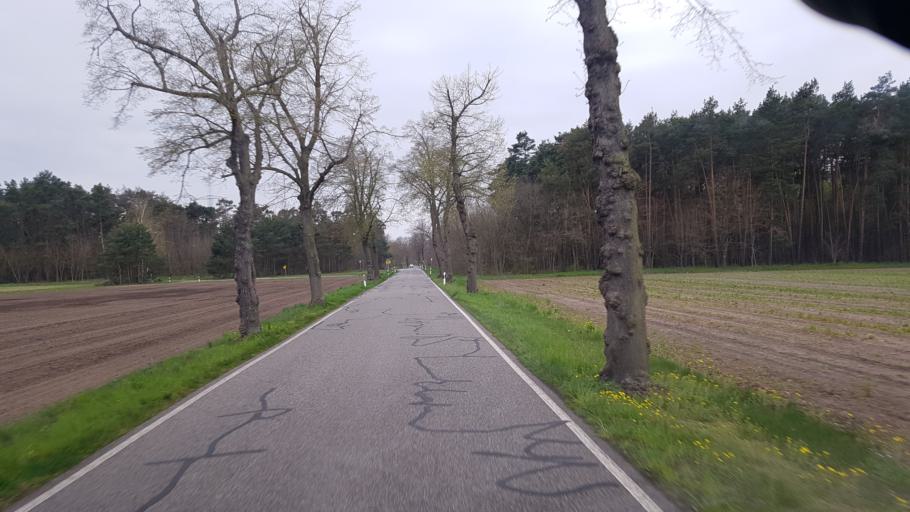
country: DE
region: Brandenburg
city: Altdobern
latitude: 51.6801
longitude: 14.0642
